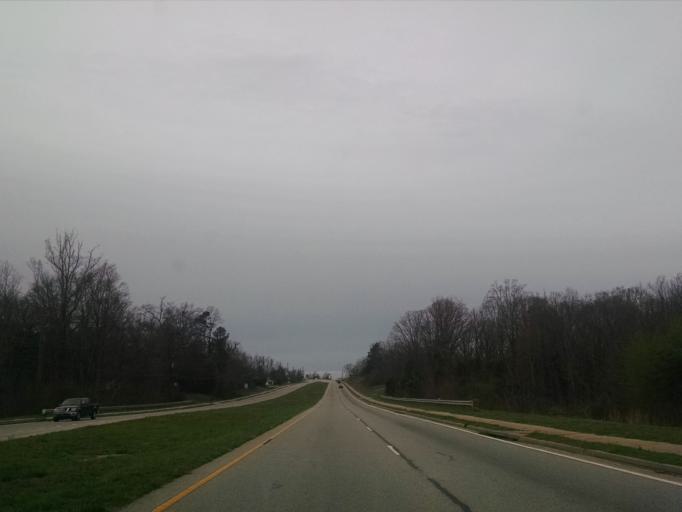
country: US
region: Georgia
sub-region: Hall County
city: Oakwood
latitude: 34.2103
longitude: -83.8575
